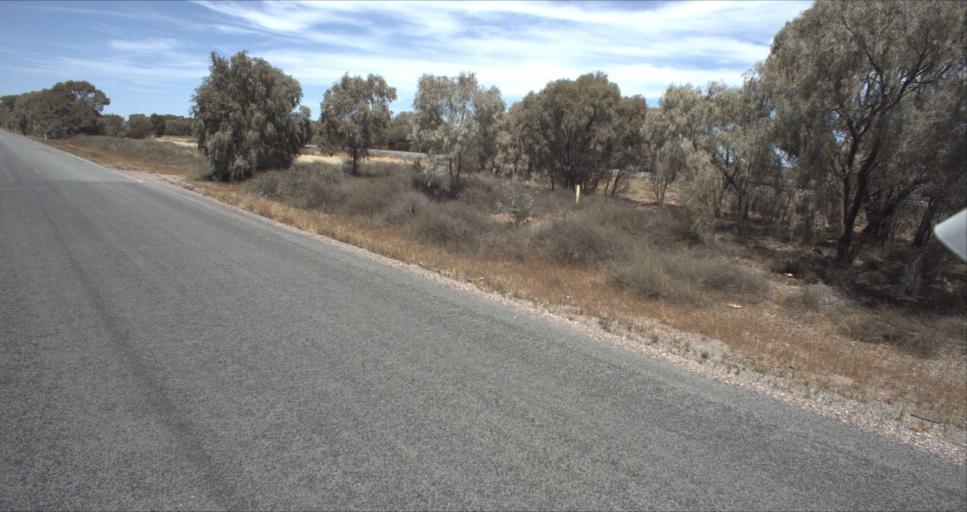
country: AU
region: New South Wales
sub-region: Leeton
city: Leeton
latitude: -34.6357
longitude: 146.4612
